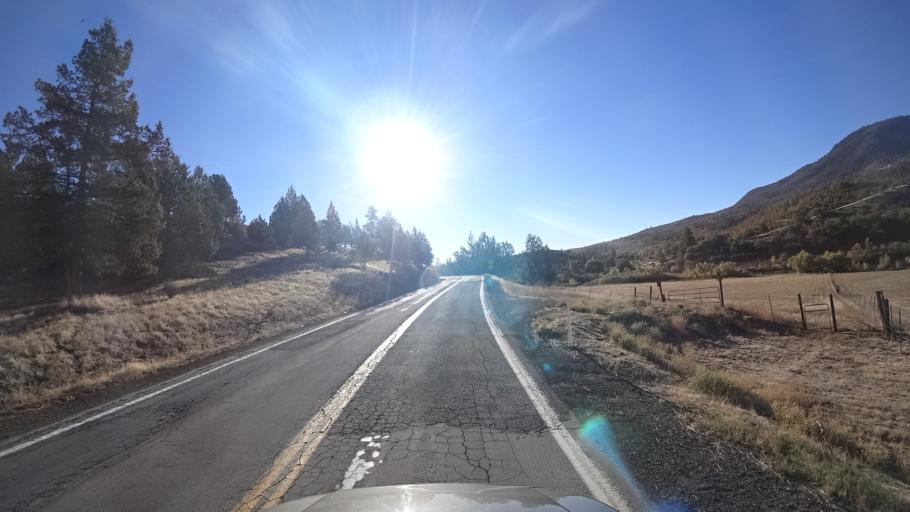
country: US
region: California
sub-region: Siskiyou County
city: Montague
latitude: 41.8995
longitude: -122.5044
